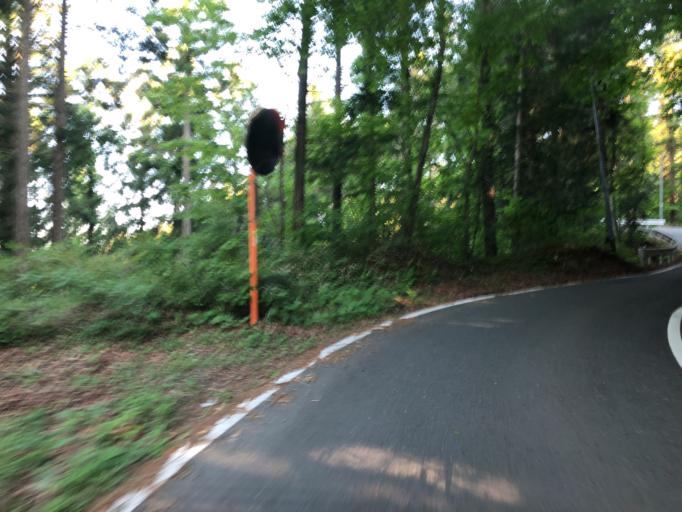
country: JP
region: Ibaraki
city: Kitaibaraki
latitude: 36.8981
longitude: 140.6152
